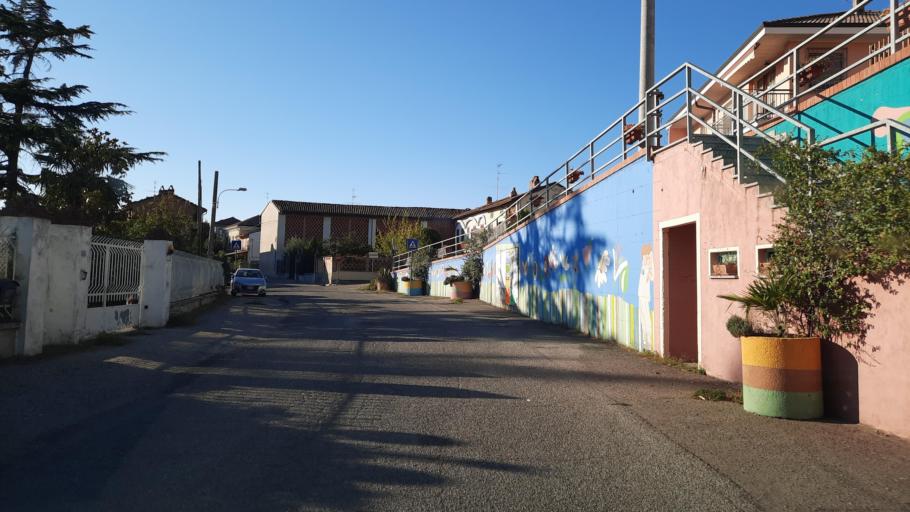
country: IT
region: Piedmont
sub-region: Provincia di Alessandria
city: Camagna Monferrato
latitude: 45.0026
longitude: 8.4168
